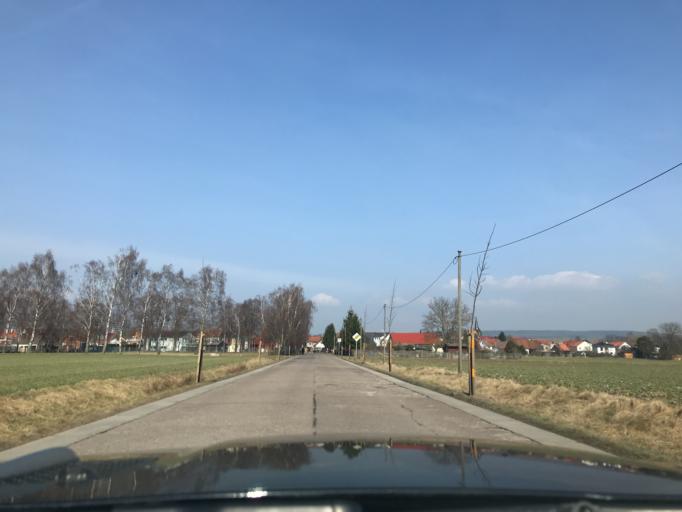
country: DE
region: Thuringia
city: Muehlhausen
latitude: 51.2080
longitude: 10.4931
